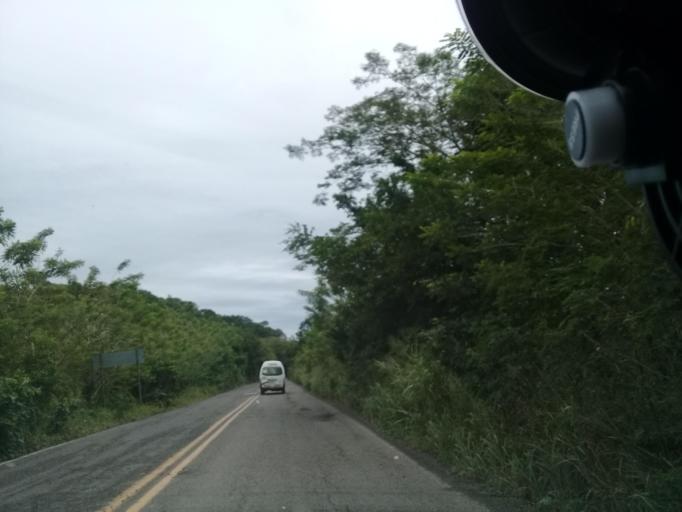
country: MX
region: Veracruz
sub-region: Chalma
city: San Pedro Coyutla
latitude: 21.2081
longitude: -98.3876
